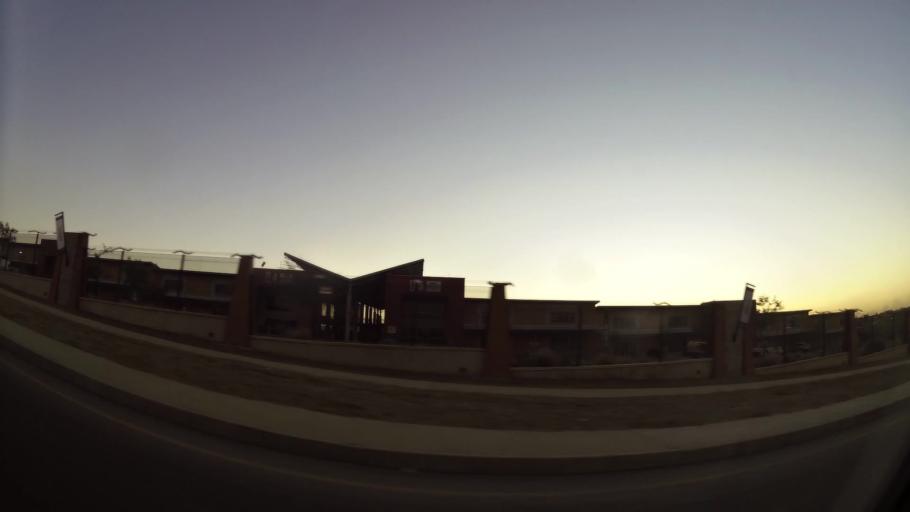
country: ZA
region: Gauteng
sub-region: City of Johannesburg Metropolitan Municipality
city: Diepsloot
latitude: -25.9640
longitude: 28.0248
